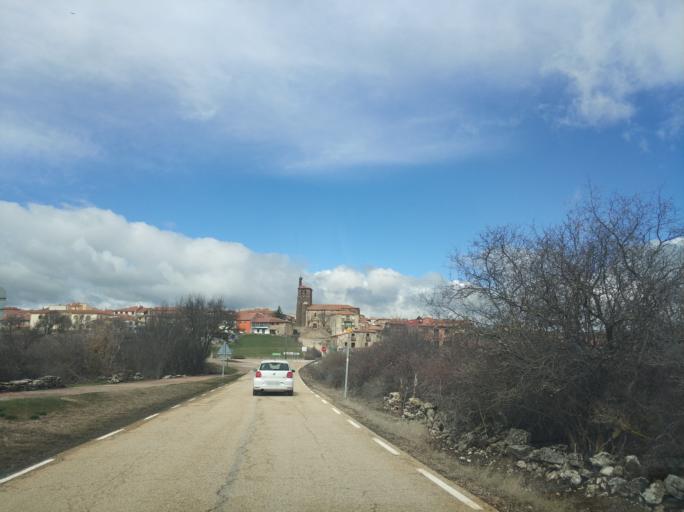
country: ES
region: Castille and Leon
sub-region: Provincia de Soria
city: Abejar
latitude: 41.8056
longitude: -2.7818
